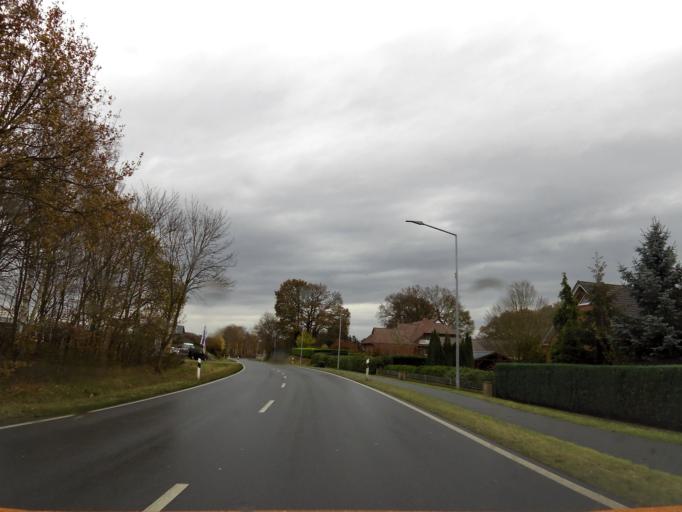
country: DE
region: Lower Saxony
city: Hude
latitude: 53.0996
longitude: 8.4868
